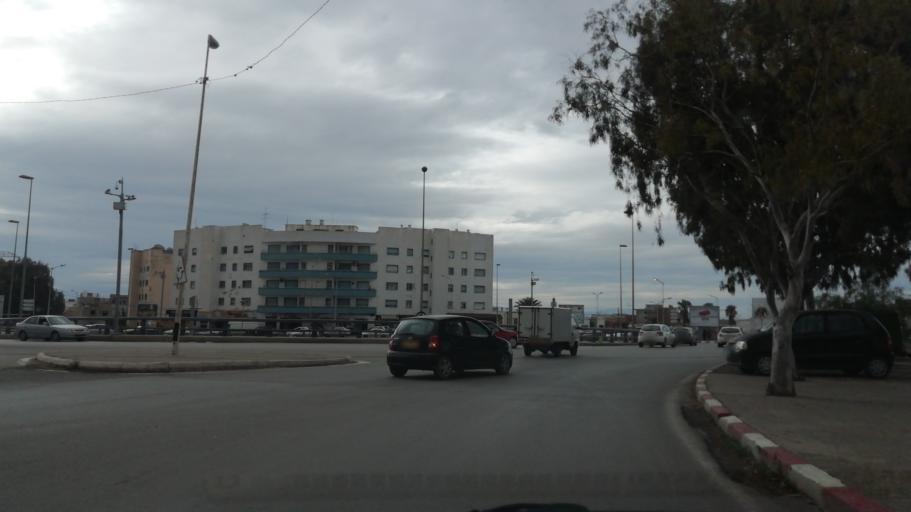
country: DZ
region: Oran
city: Oran
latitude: 35.6977
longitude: -0.6133
